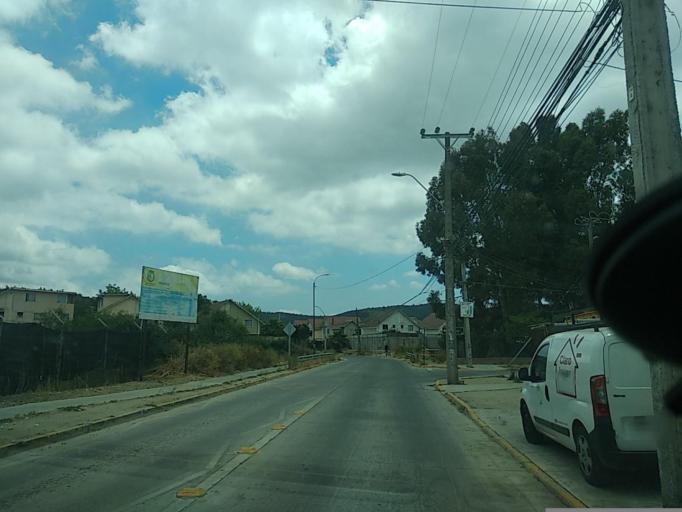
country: CL
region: Valparaiso
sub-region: Provincia de Marga Marga
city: Villa Alemana
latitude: -33.0337
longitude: -71.4056
